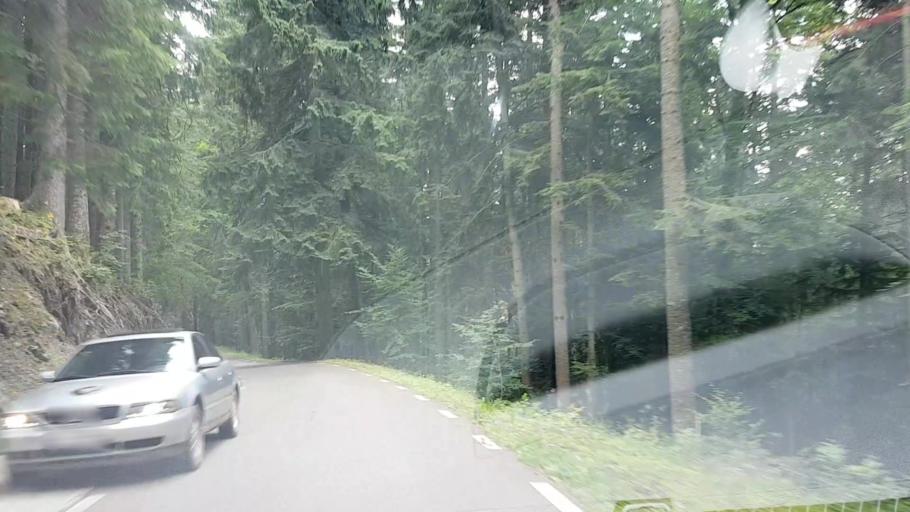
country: RO
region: Suceava
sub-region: Municipiul Campulung Moldovenesc
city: Campulung Moldovenesc
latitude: 47.4354
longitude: 25.5684
